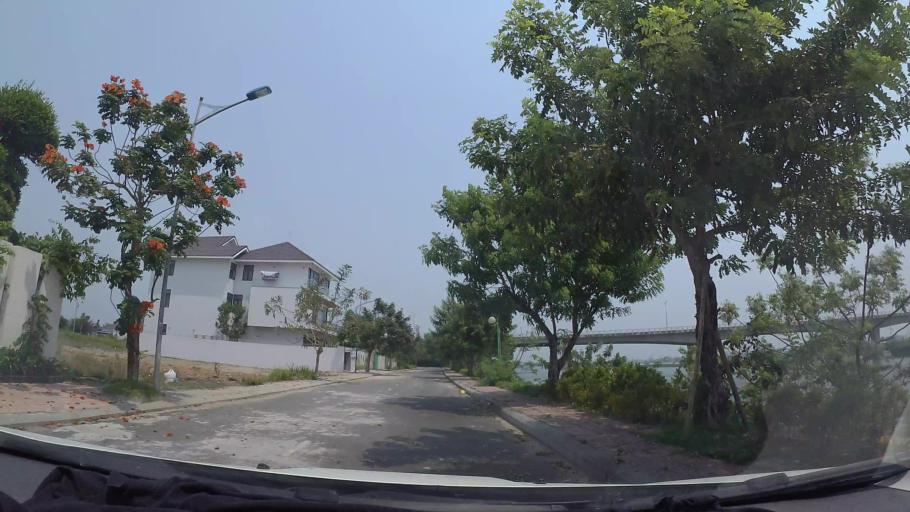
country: VN
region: Da Nang
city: Cam Le
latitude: 16.0153
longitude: 108.2123
